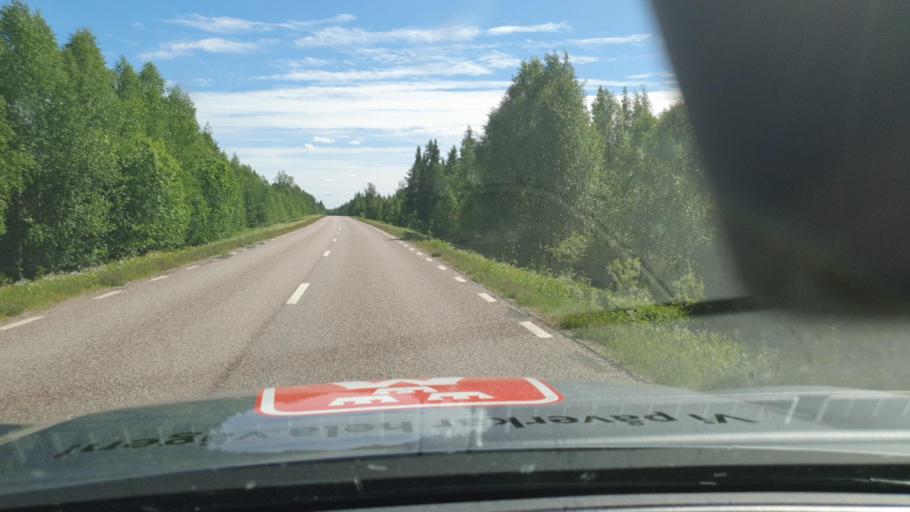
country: FI
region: Lapland
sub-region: Torniolaakso
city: Pello
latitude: 66.9168
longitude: 23.8585
